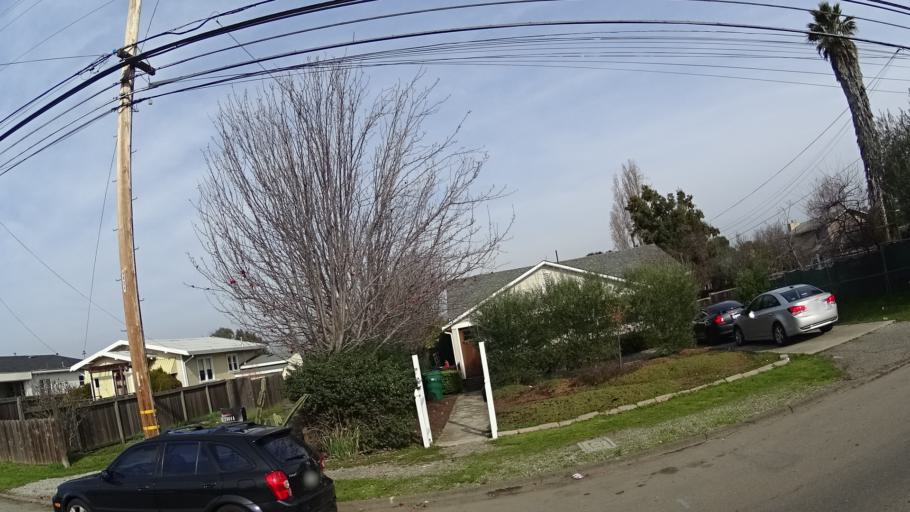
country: US
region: California
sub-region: Alameda County
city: Fairview
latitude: 37.6716
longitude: -122.0606
